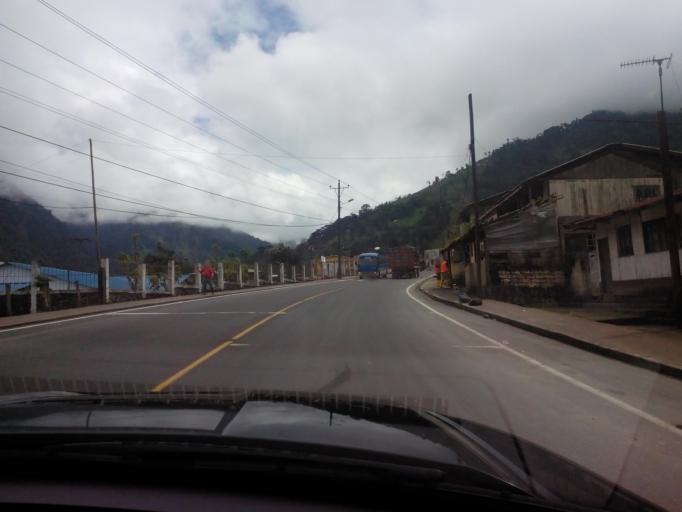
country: EC
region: Pichincha
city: Sangolqui
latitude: -0.4139
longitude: -78.0268
